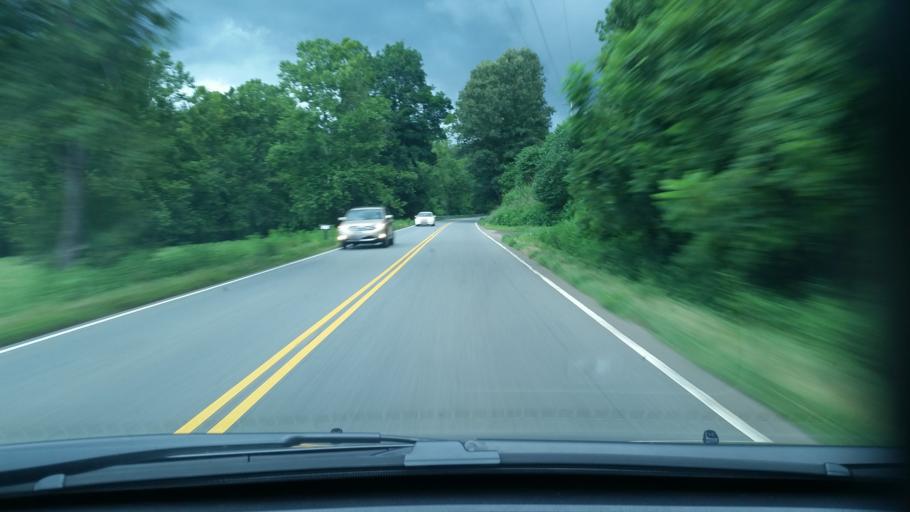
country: US
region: Virginia
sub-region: Nelson County
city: Nellysford
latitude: 37.8934
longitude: -78.8286
